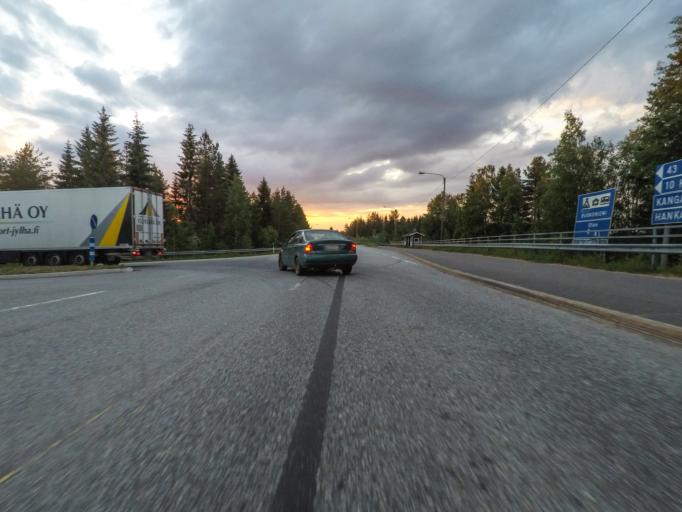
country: FI
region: Central Finland
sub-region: Jyvaeskylae
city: Hankasalmi
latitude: 62.3127
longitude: 26.4942
